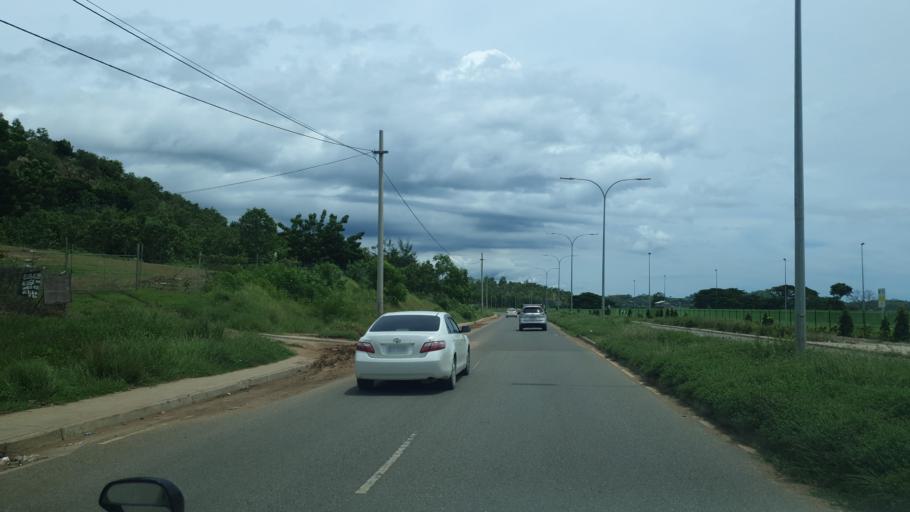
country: PG
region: National Capital
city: Port Moresby
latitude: -9.4949
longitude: 147.2253
